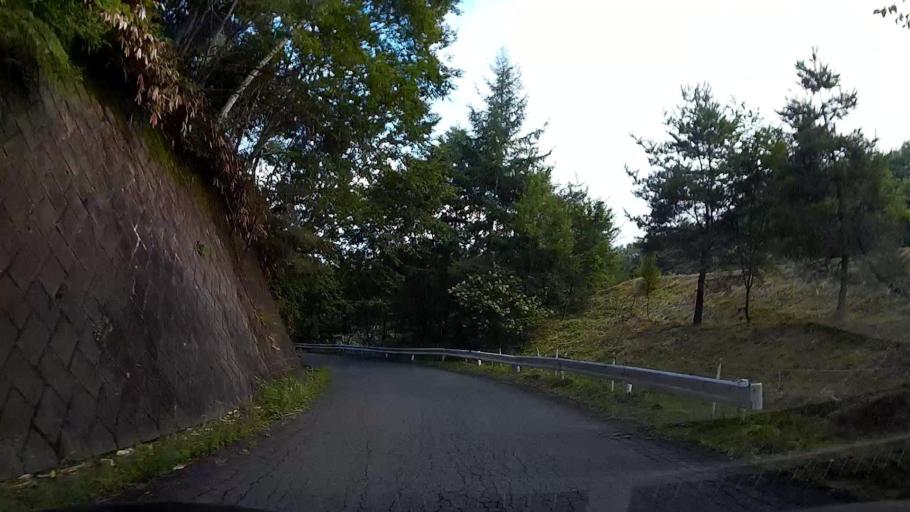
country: JP
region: Gunma
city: Nakanojomachi
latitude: 36.6280
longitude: 138.6260
